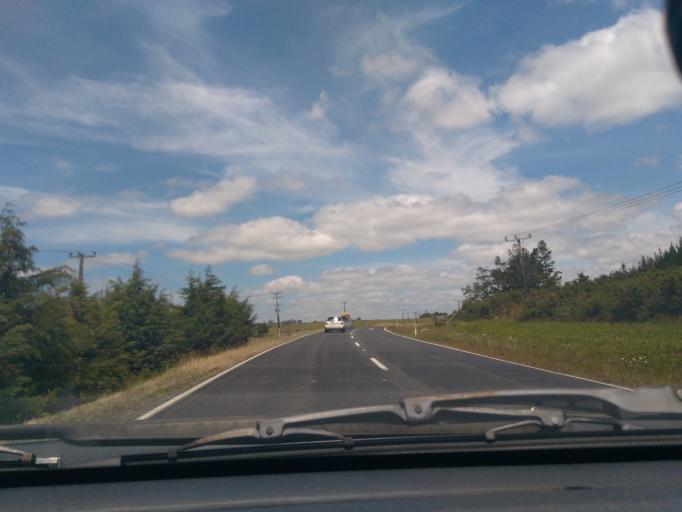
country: NZ
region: Northland
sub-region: Far North District
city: Kerikeri
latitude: -35.1223
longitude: 173.8713
